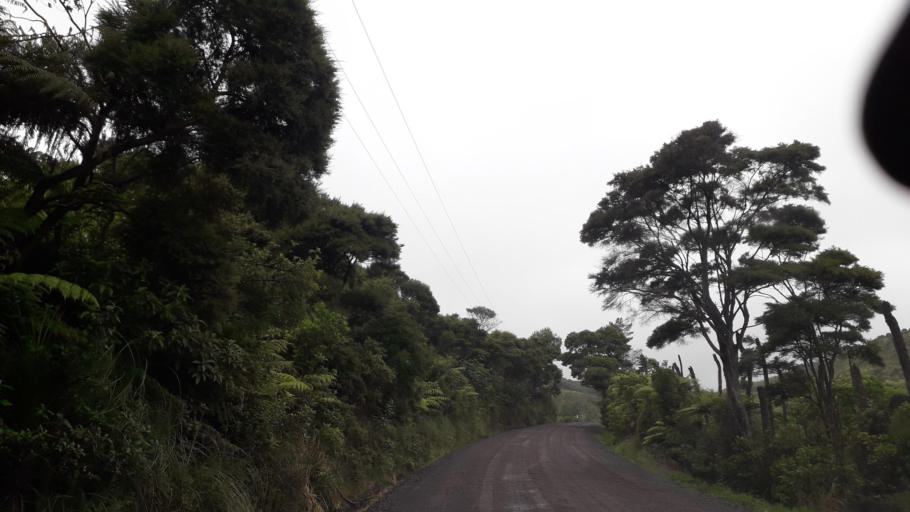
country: NZ
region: Northland
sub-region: Far North District
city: Paihia
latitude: -35.2381
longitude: 174.2517
